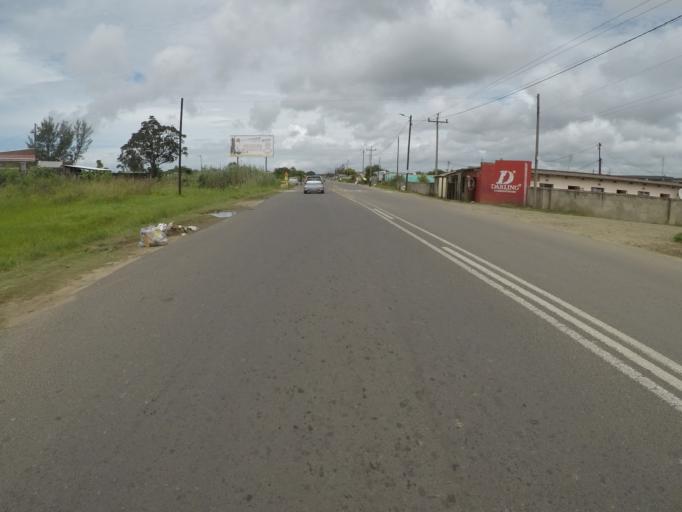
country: ZA
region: KwaZulu-Natal
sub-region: uThungulu District Municipality
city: eSikhawini
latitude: -28.8675
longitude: 31.9060
